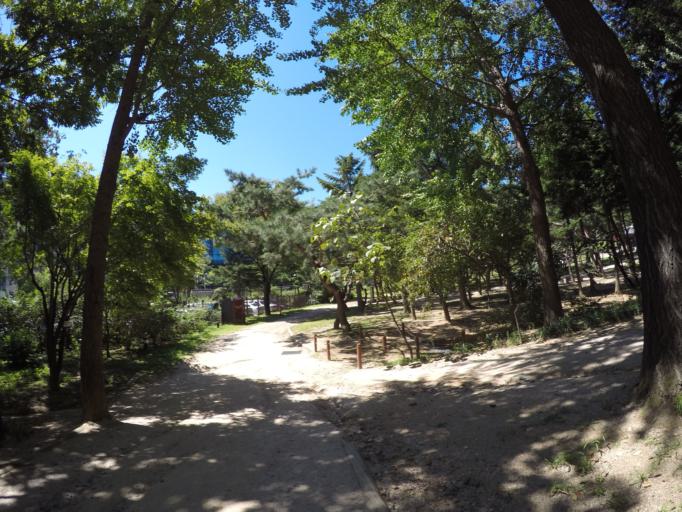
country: KR
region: Seoul
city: Seoul
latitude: 37.5075
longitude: 127.0474
